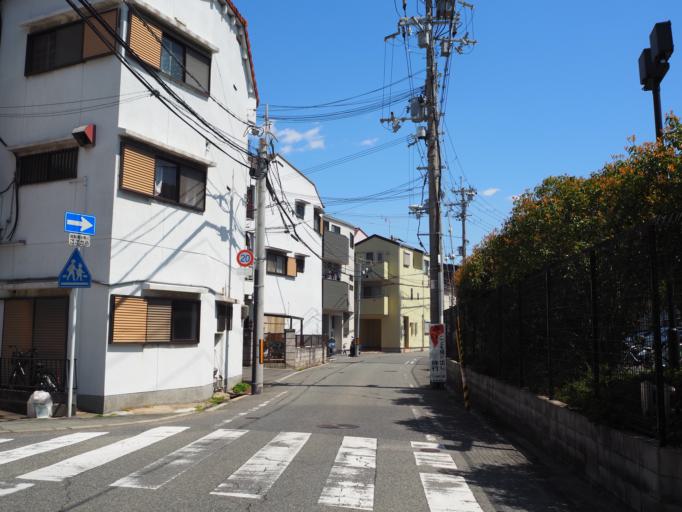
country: JP
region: Hyogo
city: Amagasaki
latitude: 34.7320
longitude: 135.4584
